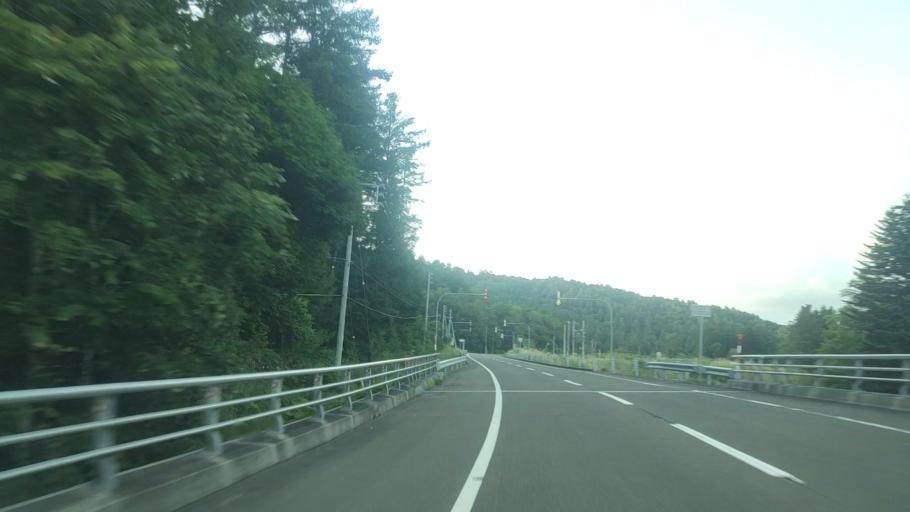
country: JP
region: Hokkaido
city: Bibai
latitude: 43.0610
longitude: 142.0996
